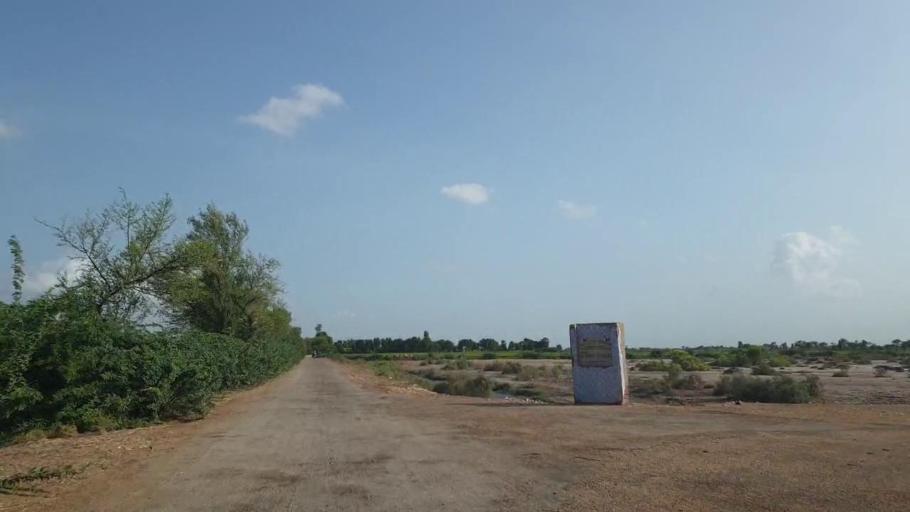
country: PK
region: Sindh
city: Kadhan
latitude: 24.6266
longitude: 69.0959
